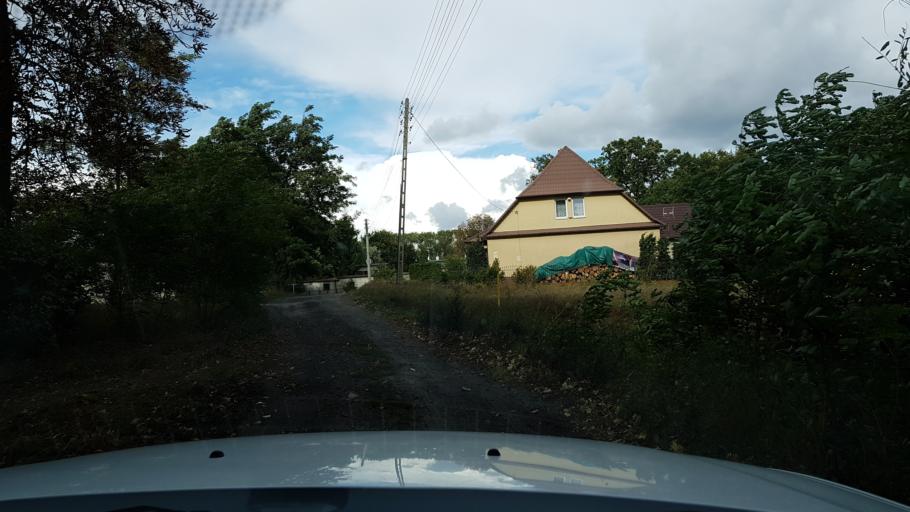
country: PL
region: West Pomeranian Voivodeship
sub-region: Powiat gryfinski
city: Gryfino
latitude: 53.3042
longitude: 14.5075
